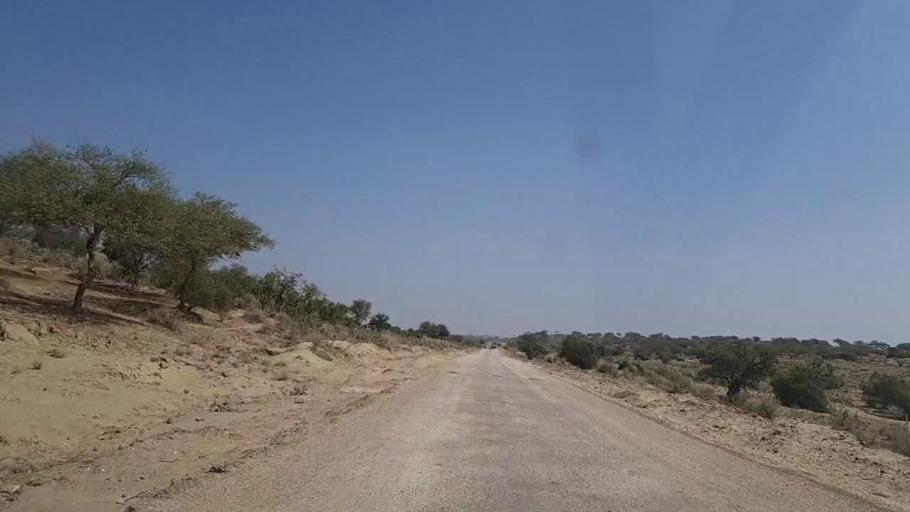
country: PK
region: Sindh
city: Diplo
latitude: 24.4781
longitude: 69.5087
